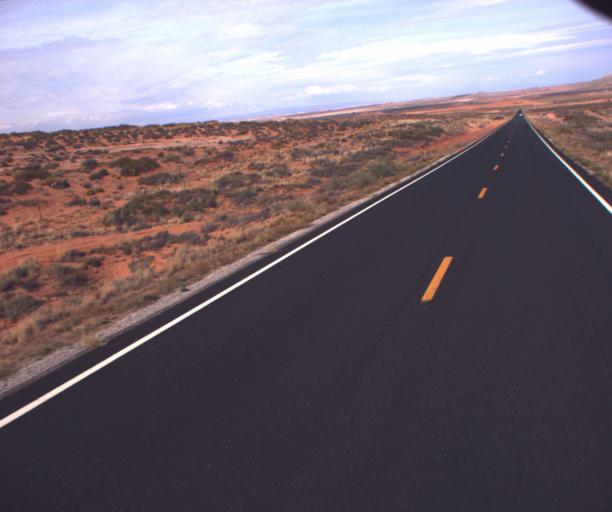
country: US
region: Arizona
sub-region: Apache County
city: Many Farms
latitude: 36.8977
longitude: -109.6258
